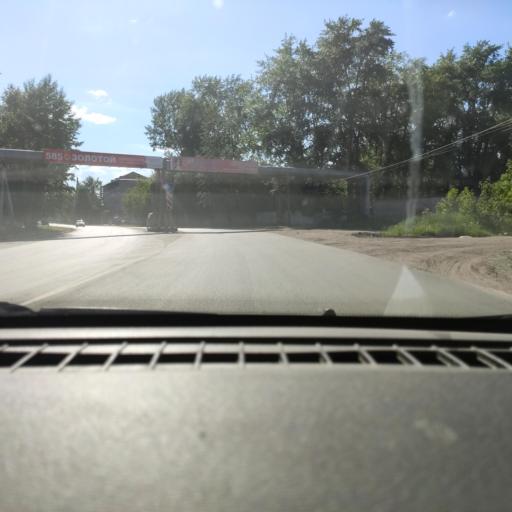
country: RU
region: Perm
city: Krasnokamsk
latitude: 58.0815
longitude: 55.7662
